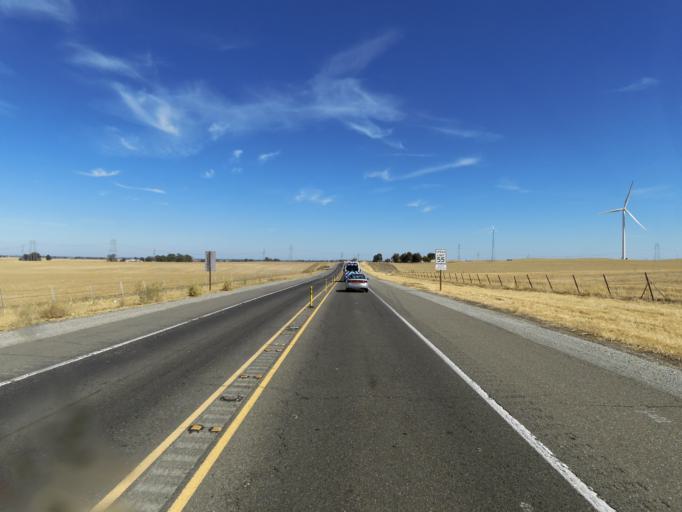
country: US
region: California
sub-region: Solano County
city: Rio Vista
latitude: 38.1834
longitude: -121.7588
